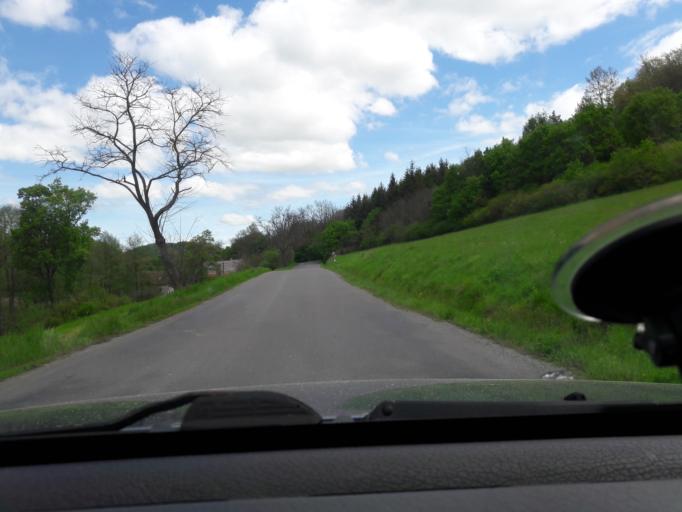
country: SK
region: Banskobystricky
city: Krupina
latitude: 48.3234
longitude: 19.0660
